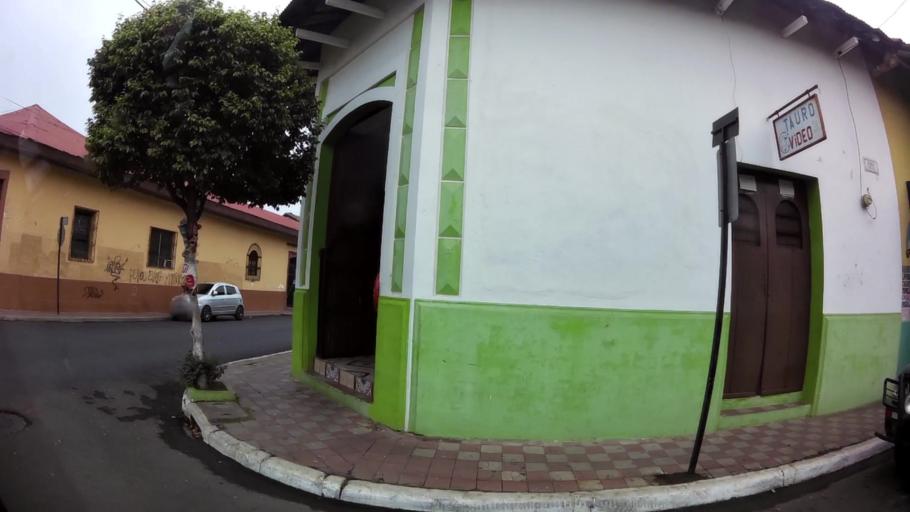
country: NI
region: Leon
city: Leon
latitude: 12.4399
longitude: -86.8785
